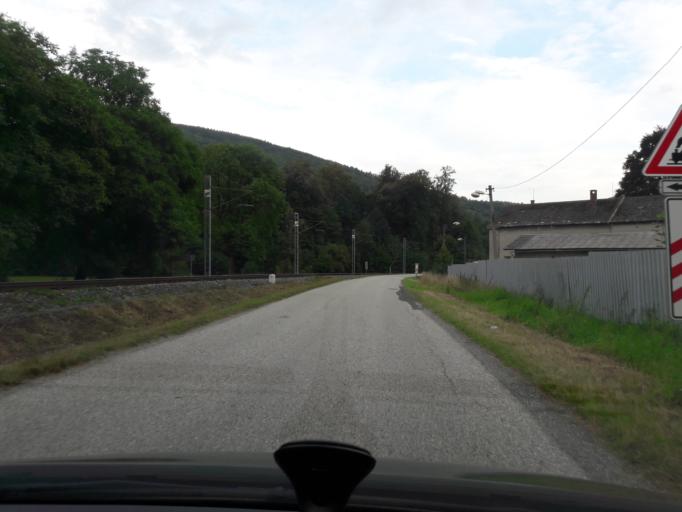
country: CZ
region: Olomoucky
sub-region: Okres Sumperk
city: Loucna nad Desnou
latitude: 50.0679
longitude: 17.0878
